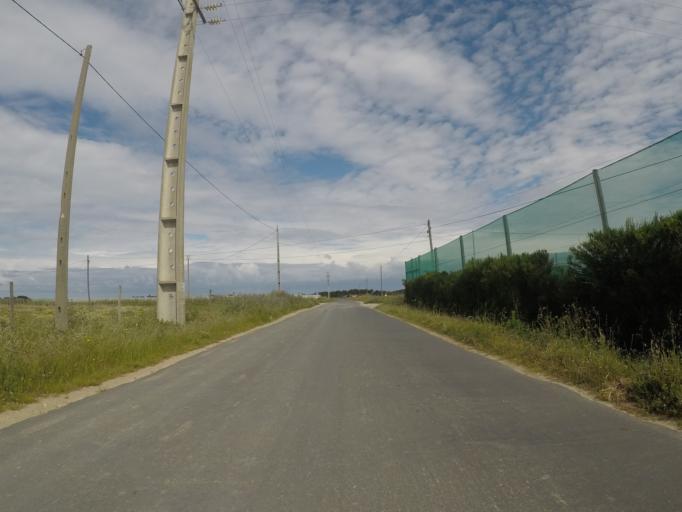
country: PT
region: Beja
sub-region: Odemira
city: Sao Teotonio
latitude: 37.4864
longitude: -8.7731
